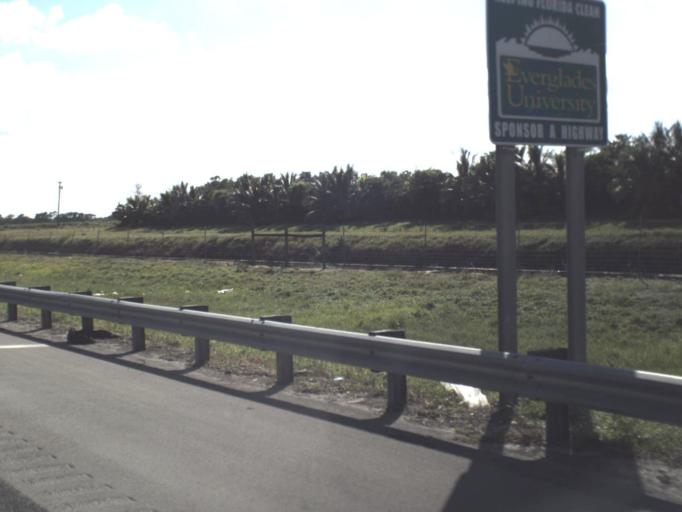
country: US
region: Florida
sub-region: Palm Beach County
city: Kings Point
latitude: 26.4262
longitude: -80.1719
